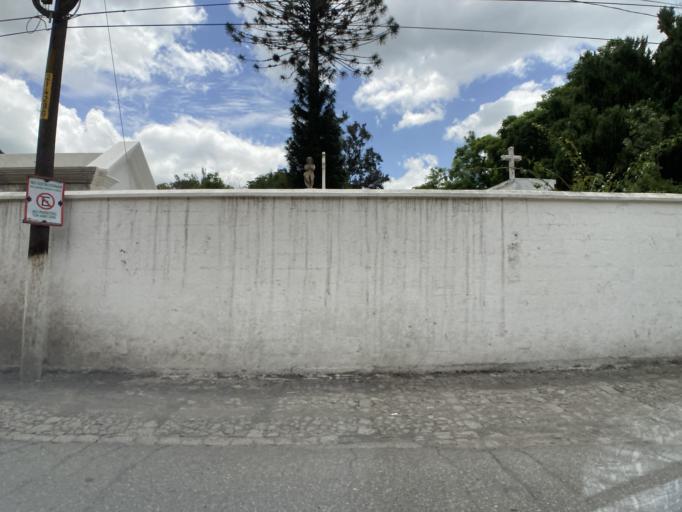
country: GT
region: Sacatepequez
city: Antigua Guatemala
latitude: 14.5558
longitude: -90.7417
